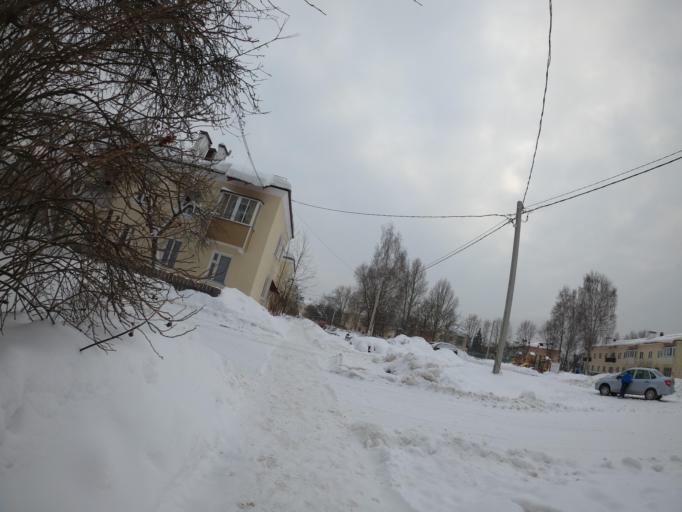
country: RU
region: Moskovskaya
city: Elektrogorsk
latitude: 55.8827
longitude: 38.7896
